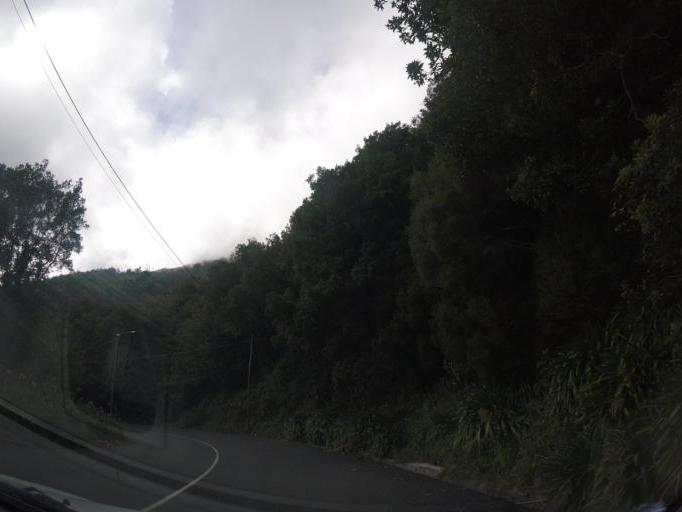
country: PT
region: Madeira
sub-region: Sao Vicente
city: Sao Vicente
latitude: 32.7511
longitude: -17.0242
